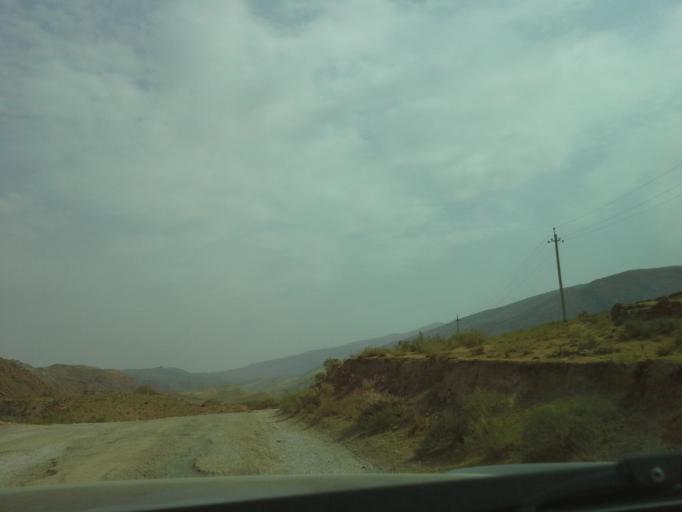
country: UZ
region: Qashqadaryo
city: Qorashina
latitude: 37.9368
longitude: 66.5175
